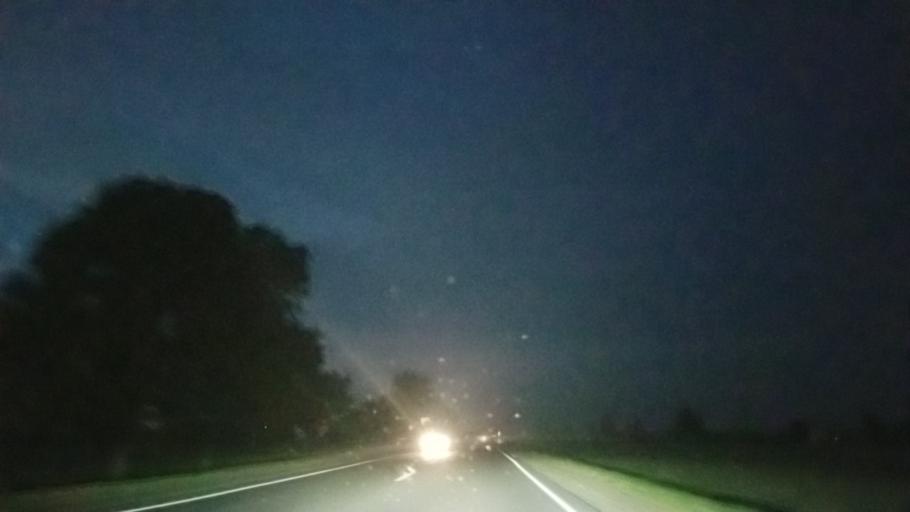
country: BY
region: Brest
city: Brest
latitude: 51.9887
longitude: 23.7051
